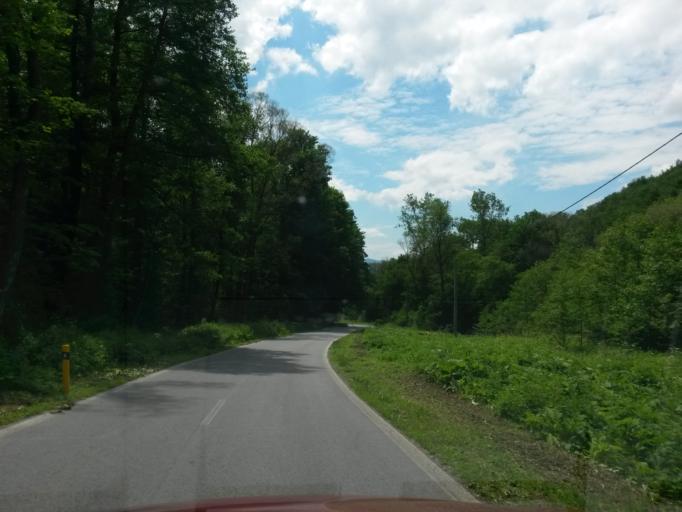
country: SK
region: Kosicky
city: Gelnica
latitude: 48.9090
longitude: 21.0294
